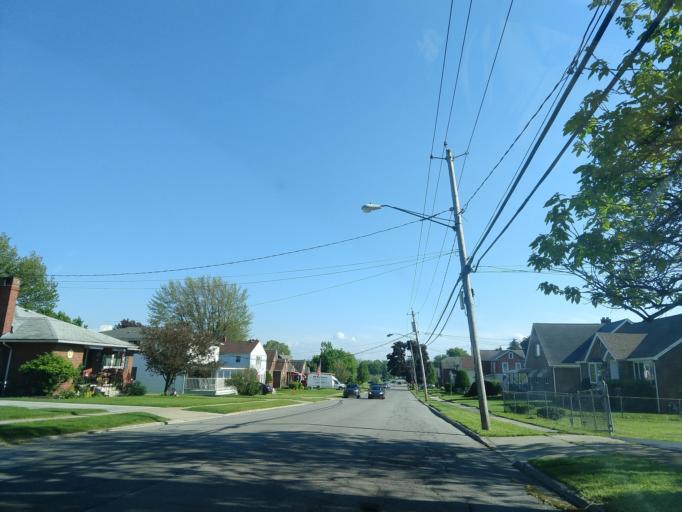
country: US
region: New York
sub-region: Erie County
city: Lackawanna
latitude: 42.8272
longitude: -78.8127
